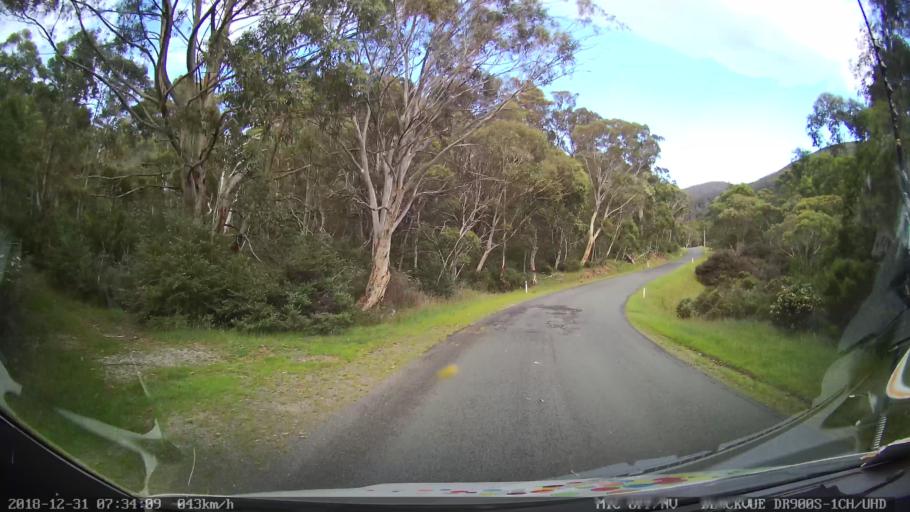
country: AU
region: New South Wales
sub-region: Snowy River
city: Jindabyne
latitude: -36.3355
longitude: 148.4536
